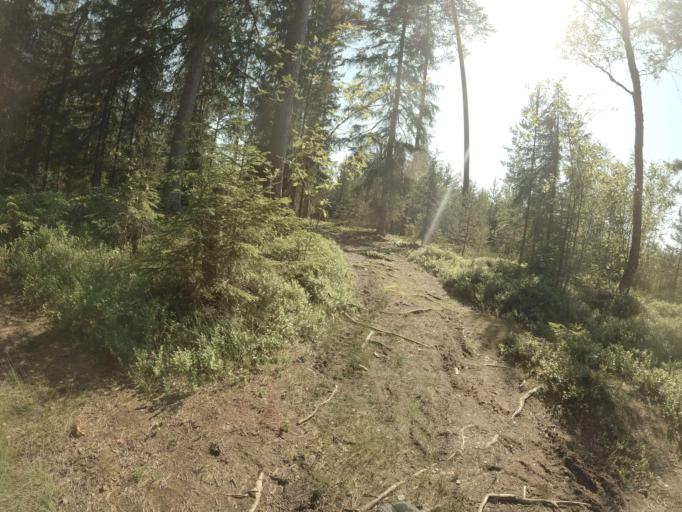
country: RU
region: Leningrad
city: Yakovlevo
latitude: 60.4633
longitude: 29.2793
